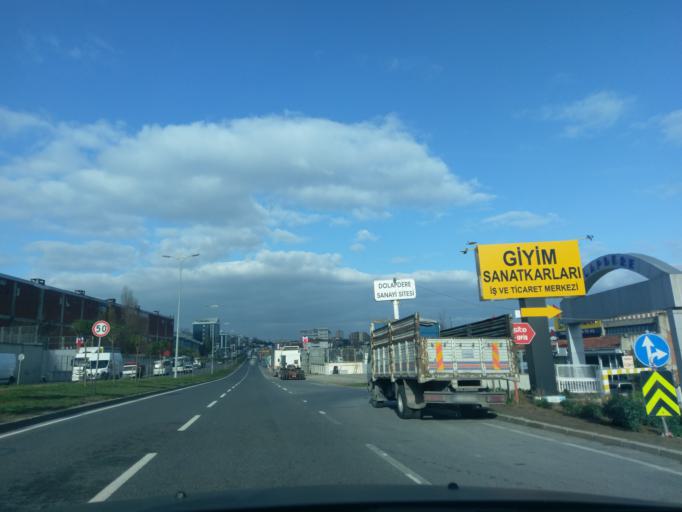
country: TR
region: Istanbul
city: Basaksehir
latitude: 41.0707
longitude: 28.8043
